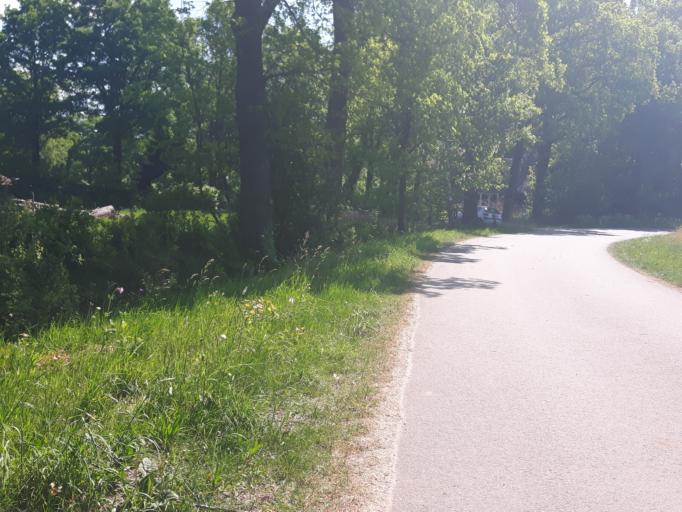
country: NL
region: Overijssel
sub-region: Gemeente Enschede
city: Enschede
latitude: 52.1783
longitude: 6.8671
